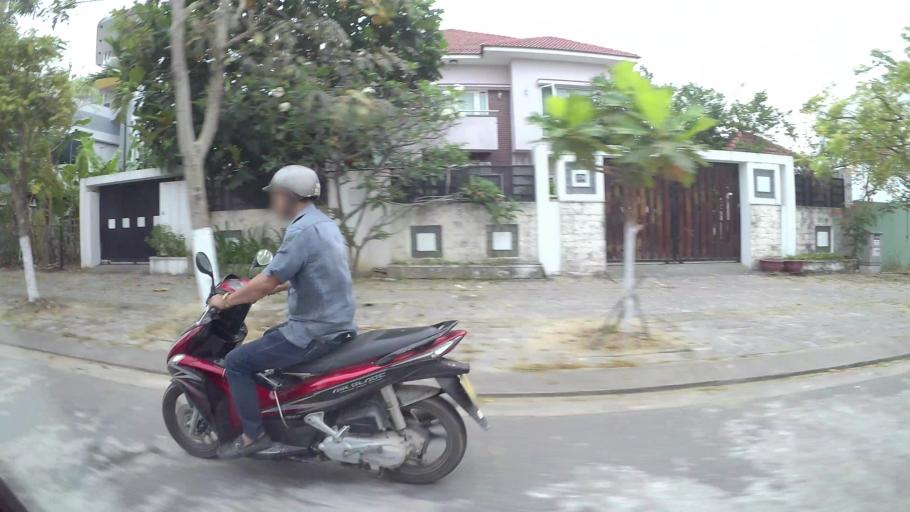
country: VN
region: Da Nang
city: Cam Le
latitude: 16.0291
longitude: 108.2263
